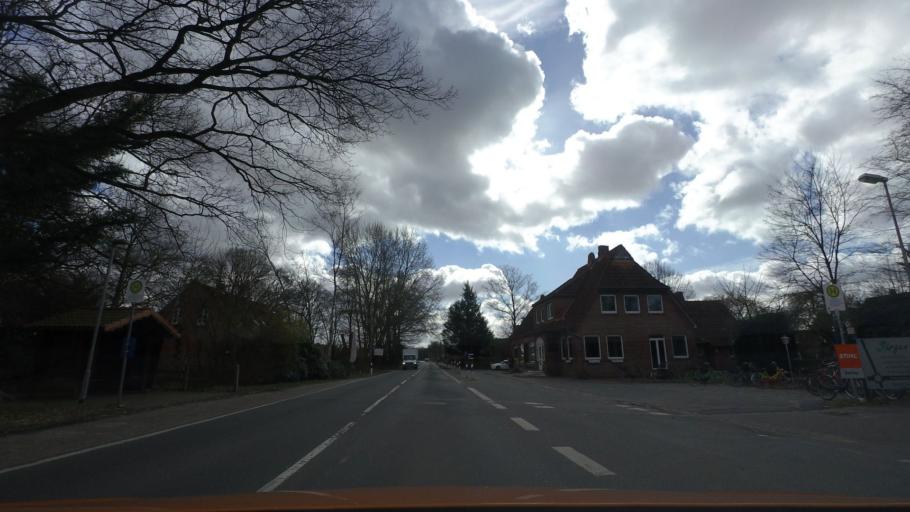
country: DE
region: Lower Saxony
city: Bad Zwischenahn
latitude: 53.1712
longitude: 8.0674
